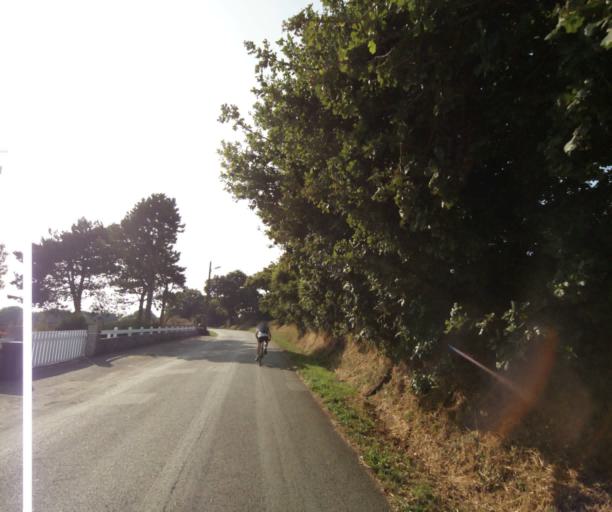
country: FR
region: Brittany
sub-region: Departement du Morbihan
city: Riantec
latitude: 47.7207
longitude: -3.3197
